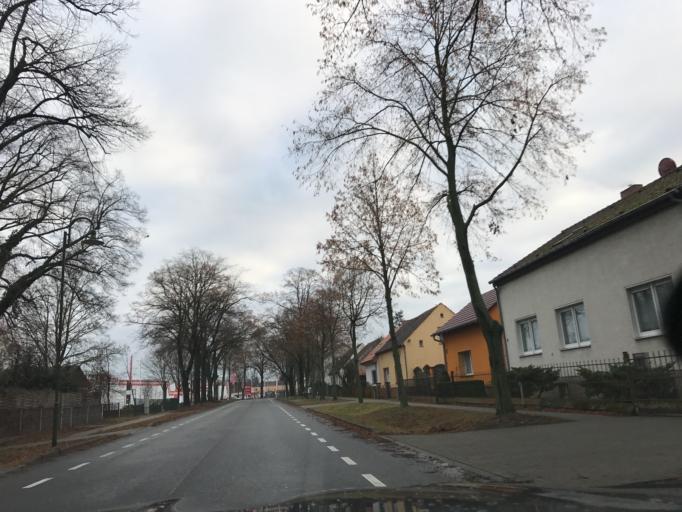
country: DE
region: Brandenburg
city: Werder
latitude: 52.3636
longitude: 12.9630
